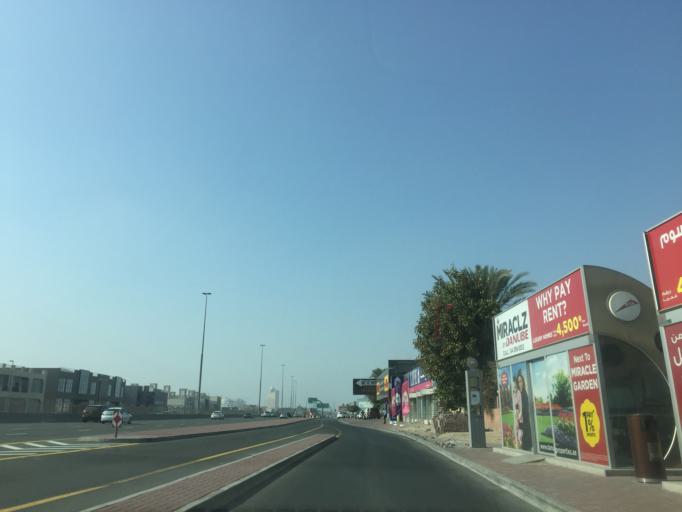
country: AE
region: Dubai
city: Dubai
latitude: 25.1073
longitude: 55.2260
